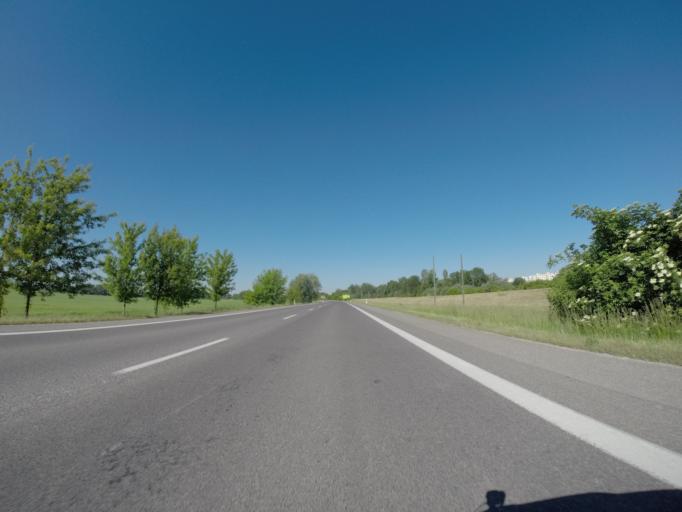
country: SK
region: Nitriansky
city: Banovce nad Bebravou
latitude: 48.5493
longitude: 18.1804
